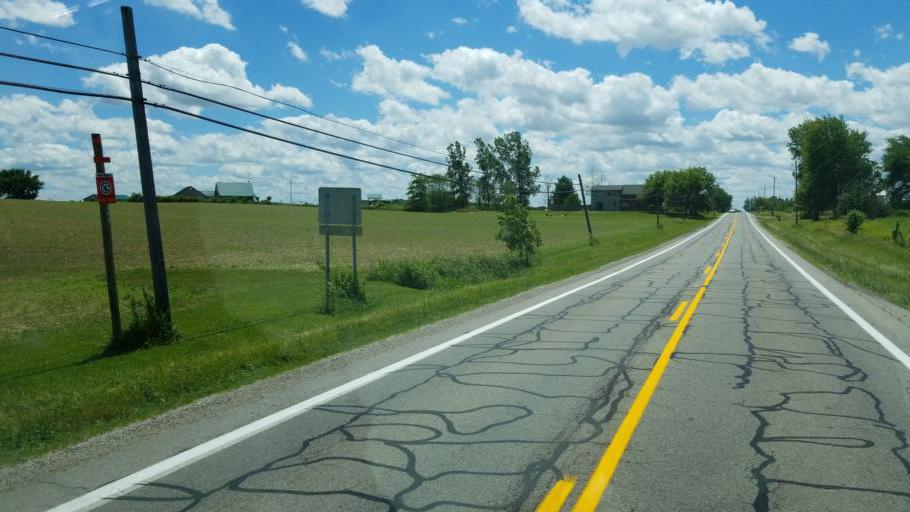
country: US
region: Ohio
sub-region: Morrow County
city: Mount Gilead
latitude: 40.6233
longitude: -82.8228
